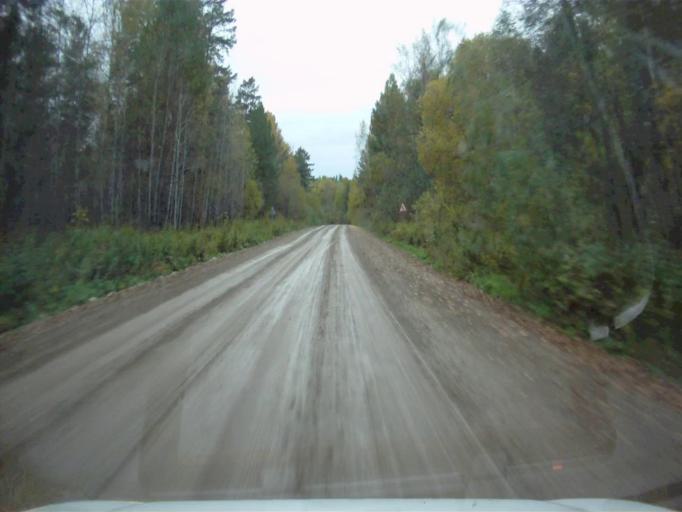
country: RU
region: Chelyabinsk
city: Nyazepetrovsk
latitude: 56.1029
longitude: 59.3867
